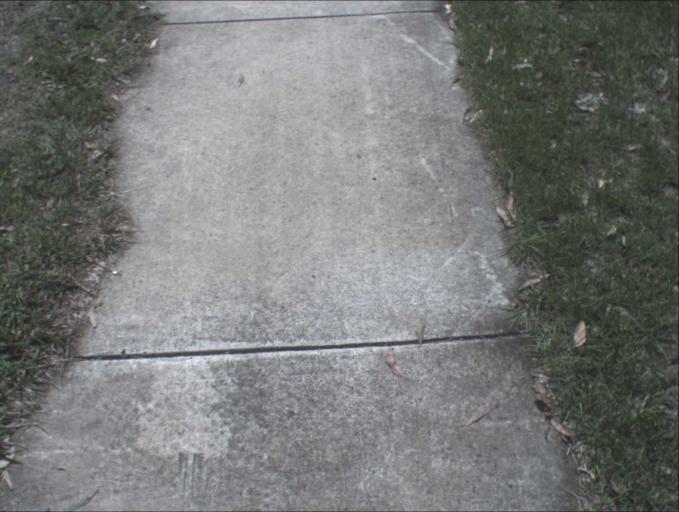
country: AU
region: Queensland
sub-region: Logan
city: North Maclean
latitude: -27.7496
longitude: 153.0144
